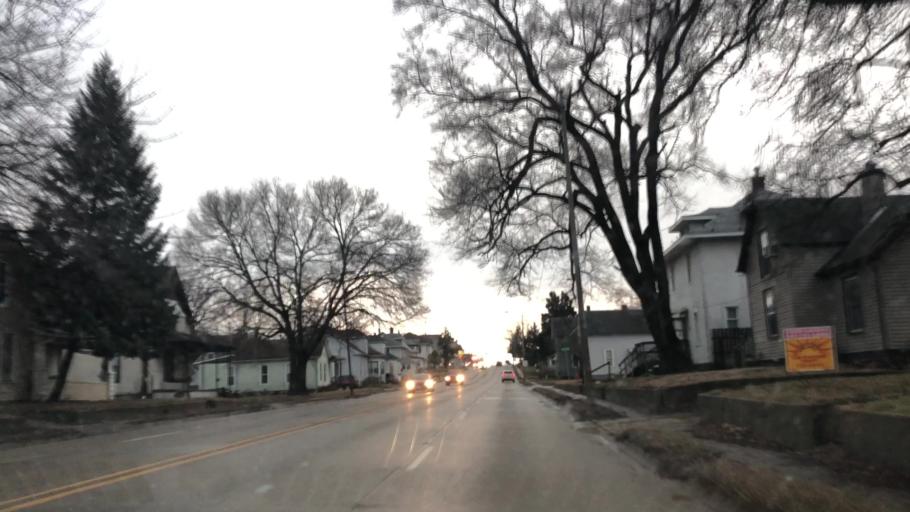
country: US
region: Iowa
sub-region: Marshall County
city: Marshalltown
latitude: 42.0540
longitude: -92.9081
